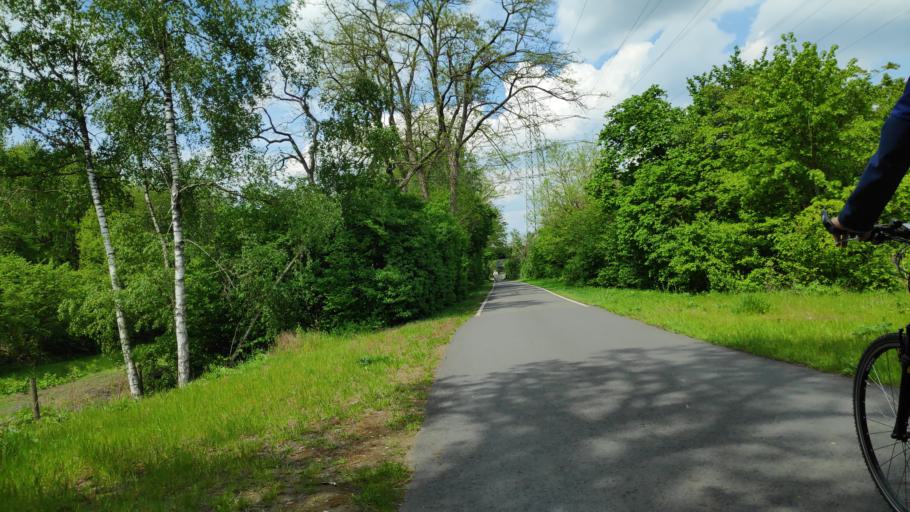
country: DE
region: North Rhine-Westphalia
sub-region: Regierungsbezirk Munster
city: Gelsenkirchen
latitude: 51.5364
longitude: 7.1300
